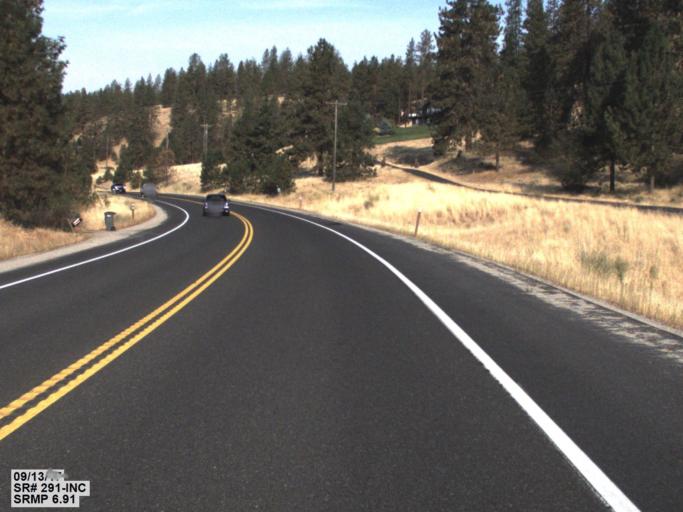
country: US
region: Washington
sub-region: Spokane County
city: Fairwood
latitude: 47.7584
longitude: -117.5206
